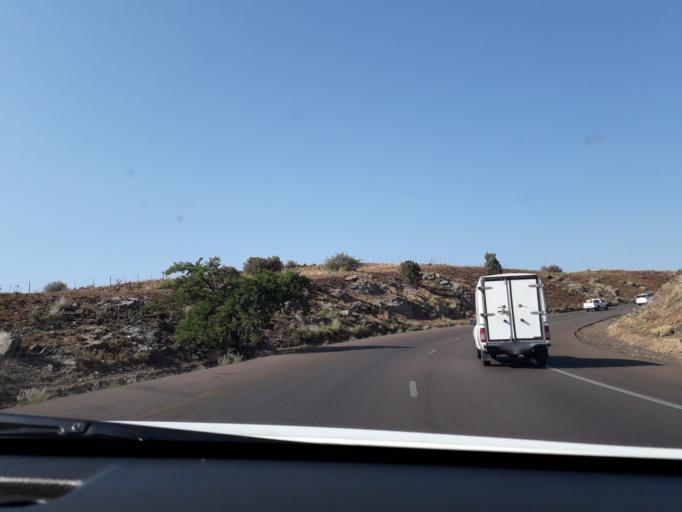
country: ZA
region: Gauteng
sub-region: City of Tshwane Metropolitan Municipality
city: Pretoria
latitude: -25.7848
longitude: 28.1924
